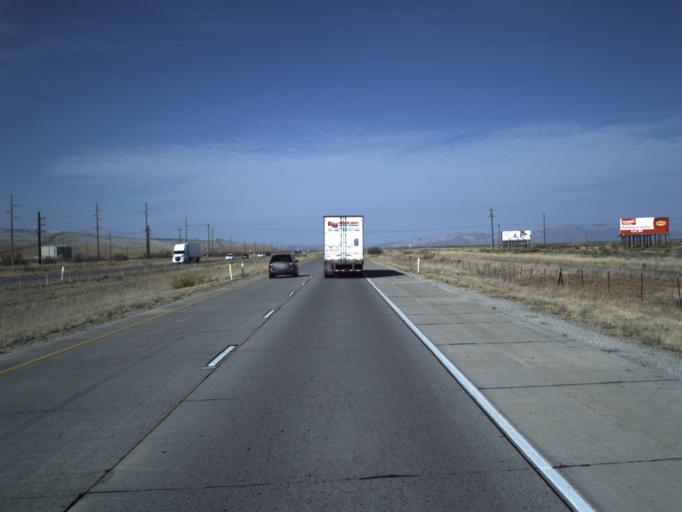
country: US
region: Utah
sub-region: Salt Lake County
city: Magna
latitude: 40.7711
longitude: -112.0952
